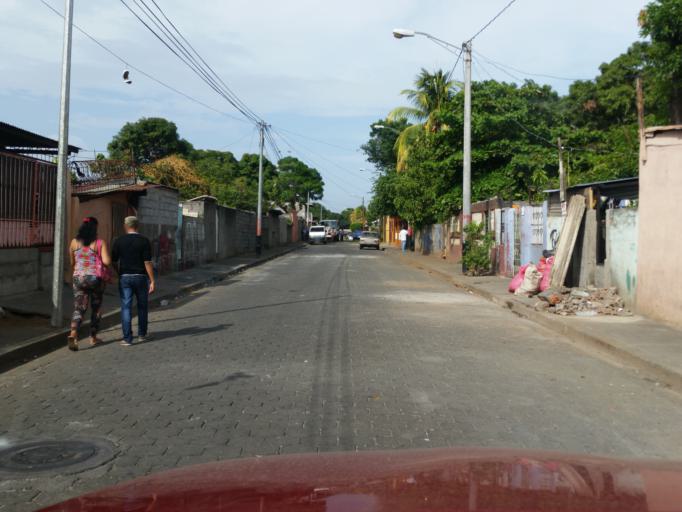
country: NI
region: Managua
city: Managua
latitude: 12.1267
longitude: -86.2532
